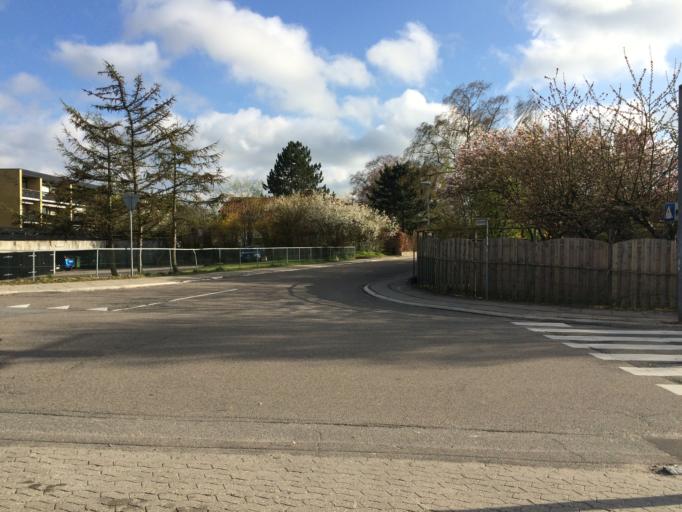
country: DK
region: Capital Region
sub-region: Egedal Kommune
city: Stenlose
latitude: 55.7676
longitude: 12.1948
